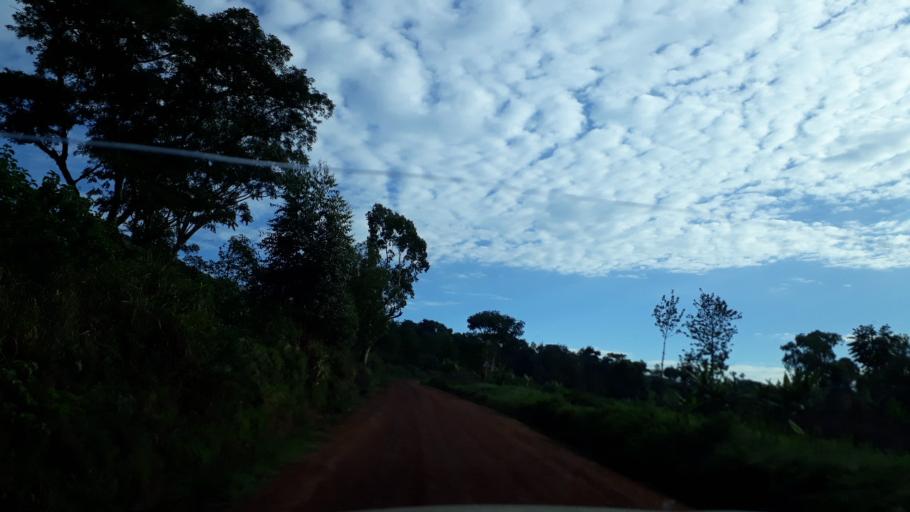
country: UG
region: Northern Region
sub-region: Zombo District
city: Paidha
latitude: 2.2567
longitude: 30.8745
